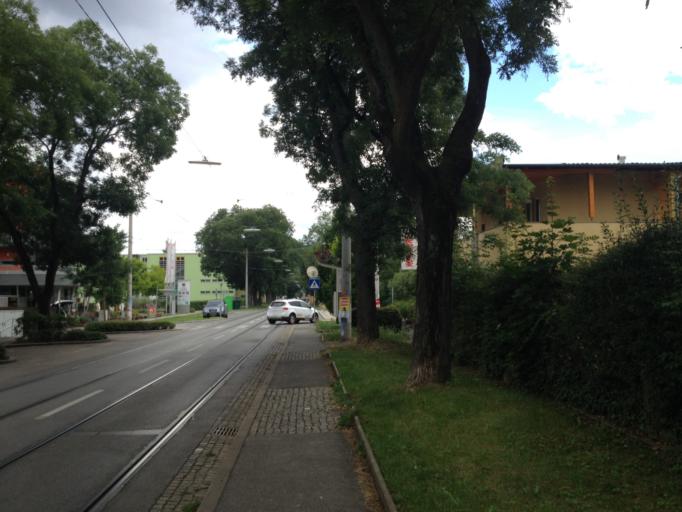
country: AT
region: Styria
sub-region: Graz Stadt
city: Graz
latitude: 47.0892
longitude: 15.4283
